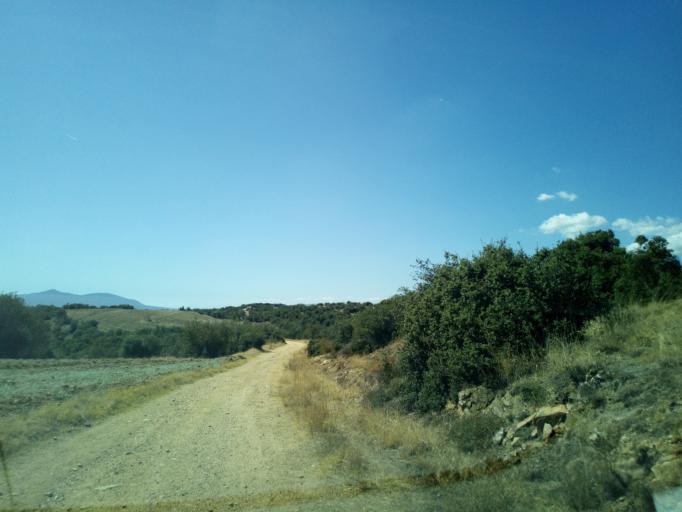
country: GR
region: Central Macedonia
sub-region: Nomos Thessalonikis
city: Gerakarou
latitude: 40.7250
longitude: 23.2298
